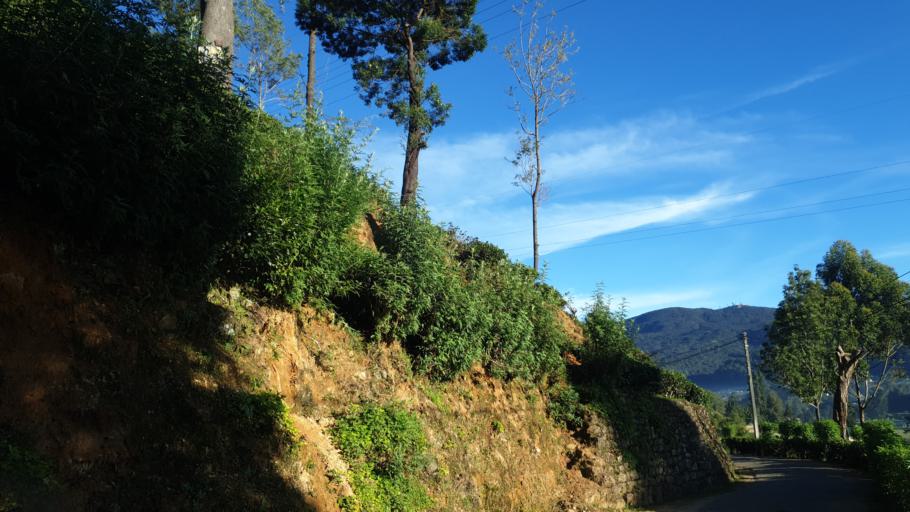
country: LK
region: Central
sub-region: Nuwara Eliya District
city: Nuwara Eliya
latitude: 6.9574
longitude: 80.7663
